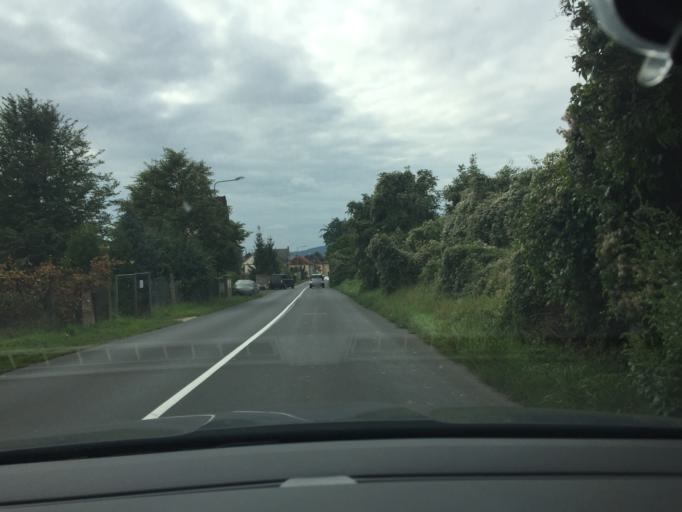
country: CZ
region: Ustecky
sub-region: Okres Litomerice
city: Litomerice
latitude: 50.5256
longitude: 14.1002
